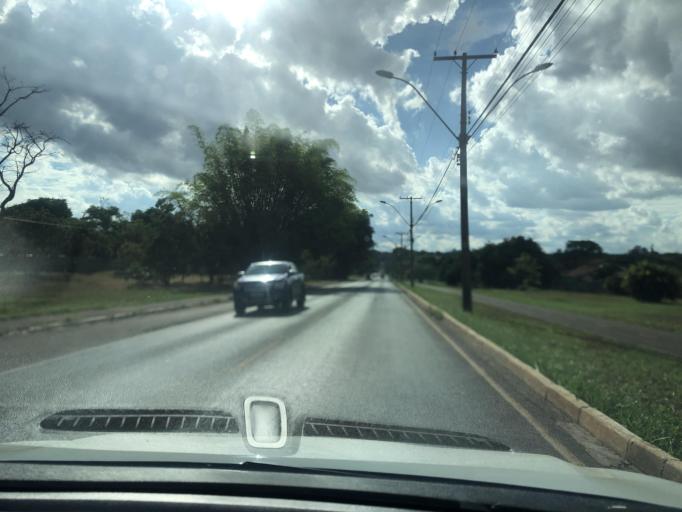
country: BR
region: Federal District
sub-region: Brasilia
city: Brasilia
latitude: -15.8976
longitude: -47.9346
